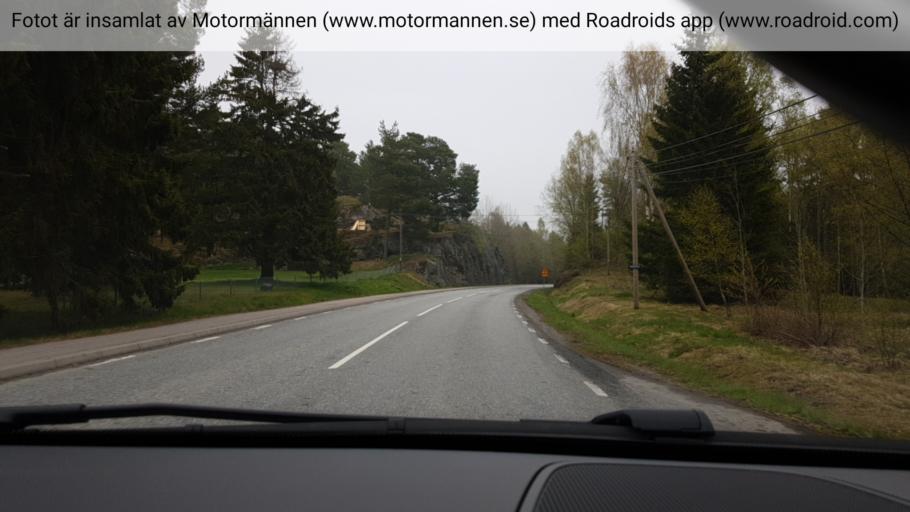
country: SE
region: Stockholm
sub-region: Nynashamns Kommun
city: Osmo
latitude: 58.9771
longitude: 17.9206
